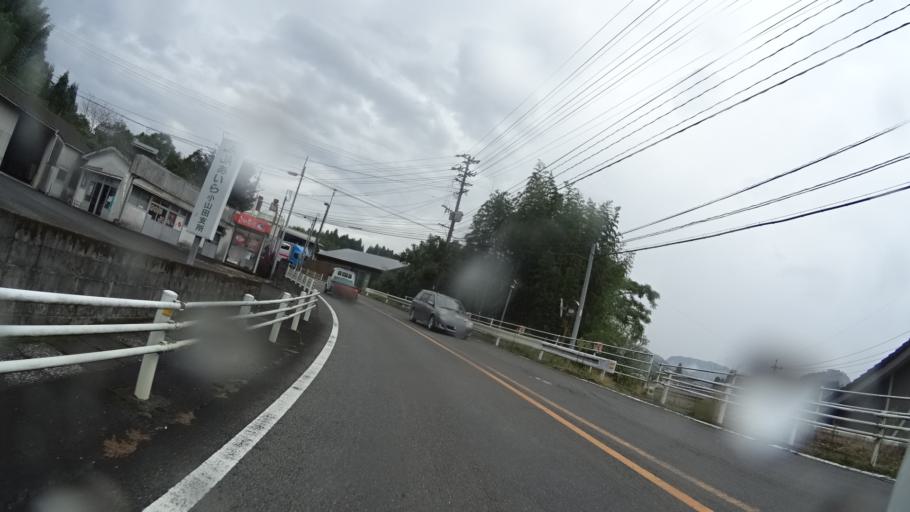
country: JP
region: Kagoshima
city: Kajiki
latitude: 31.7607
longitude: 130.6741
